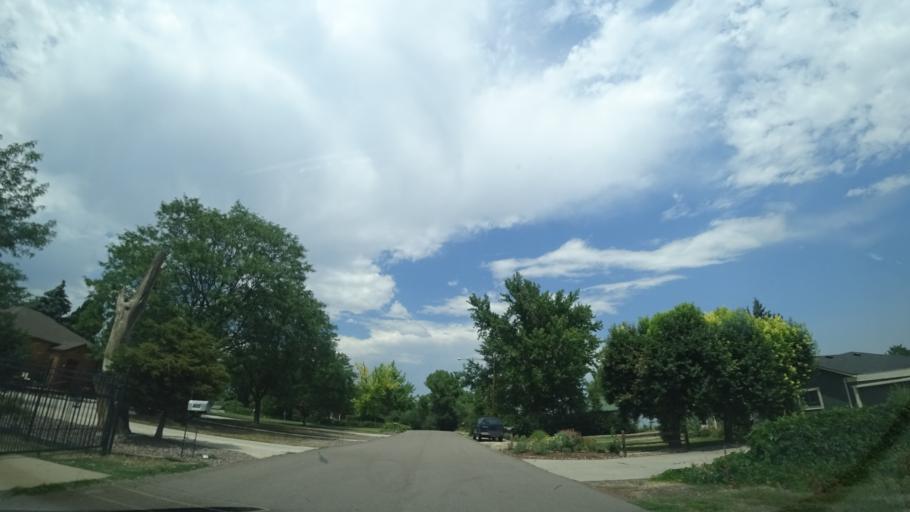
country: US
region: Colorado
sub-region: Jefferson County
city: Lakewood
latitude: 39.7225
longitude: -105.0886
